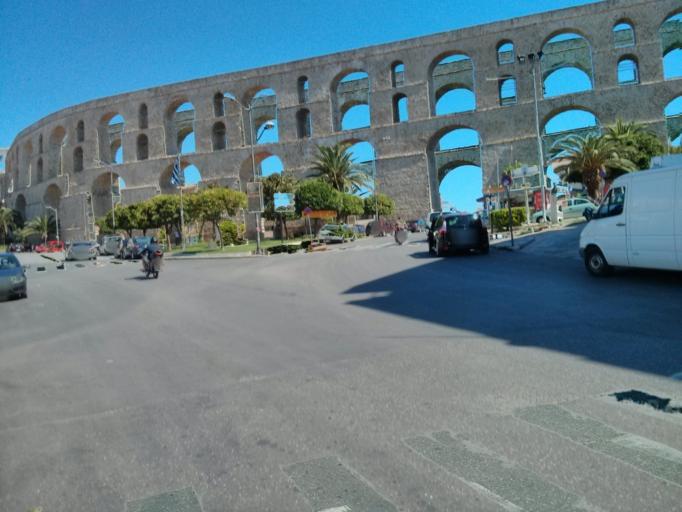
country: GR
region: East Macedonia and Thrace
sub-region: Nomos Kavalas
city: Kavala
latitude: 40.9366
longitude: 24.4147
